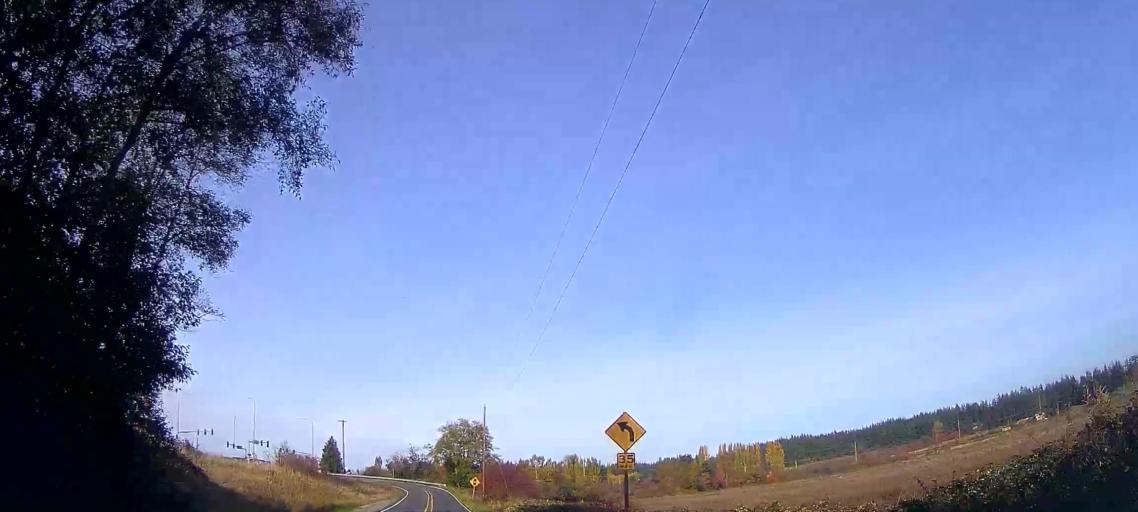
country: US
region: Washington
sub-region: Snohomish County
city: Stanwood
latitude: 48.2386
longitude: -122.4547
